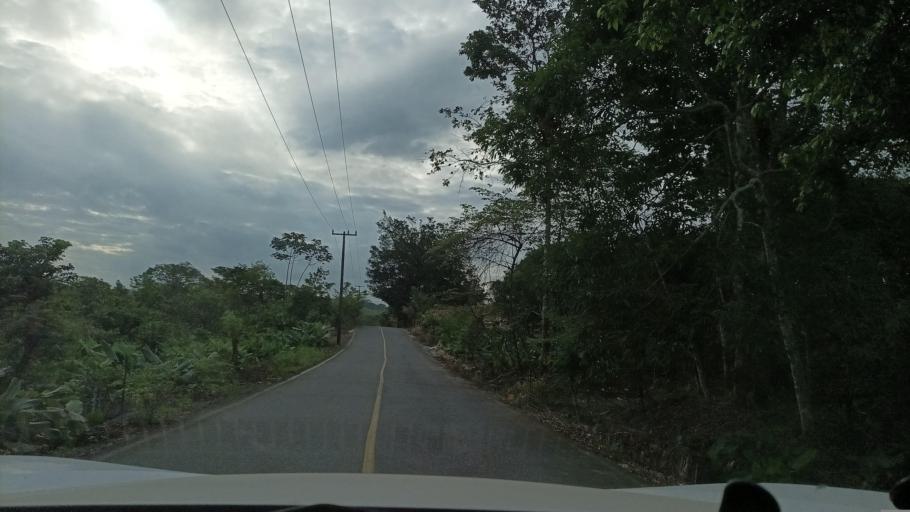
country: MX
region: Veracruz
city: Hidalgotitlan
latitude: 17.7143
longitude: -94.4721
